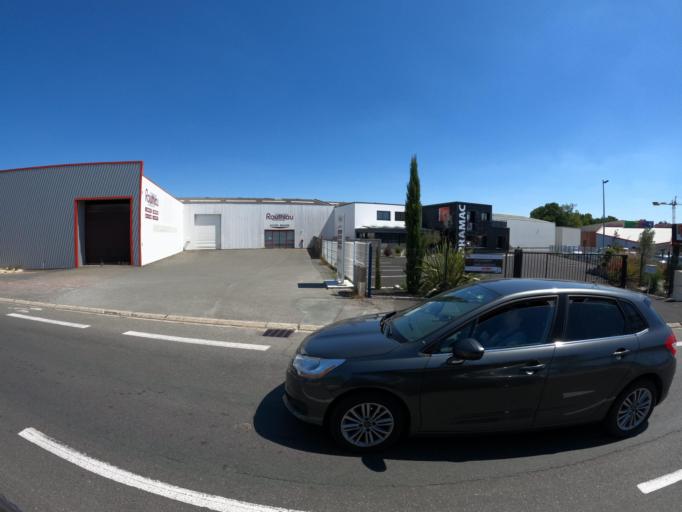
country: FR
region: Pays de la Loire
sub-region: Departement de la Vendee
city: Challans
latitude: 46.8499
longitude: -1.8591
